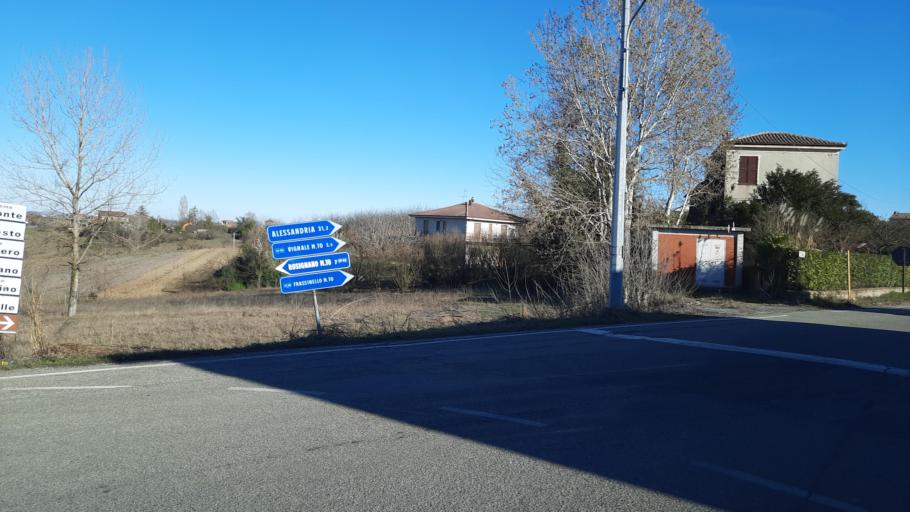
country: IT
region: Piedmont
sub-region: Provincia di Alessandria
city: Frassinello Monferrato
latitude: 45.0385
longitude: 8.3805
